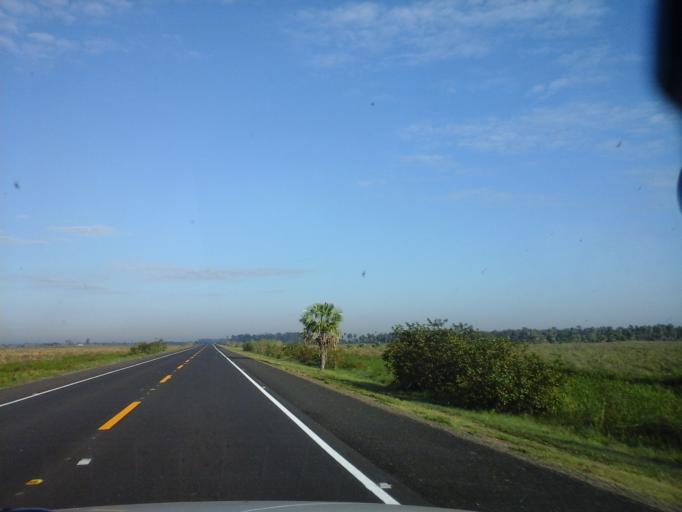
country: PY
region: Neembucu
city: Cerrito
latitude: -26.8682
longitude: -57.7892
